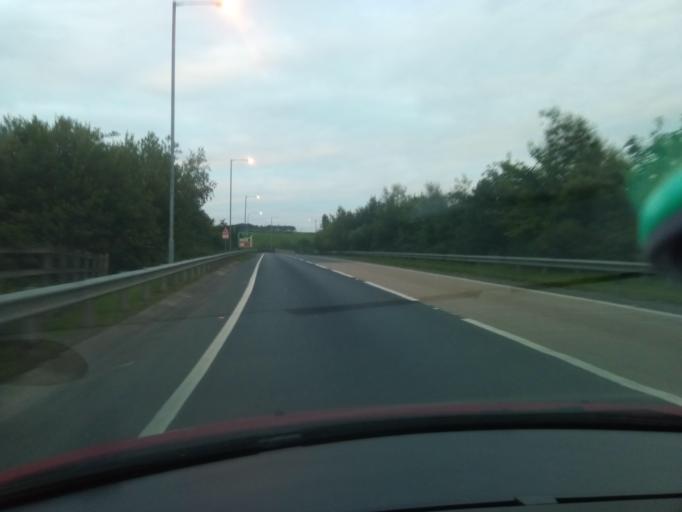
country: GB
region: England
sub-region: Northumberland
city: Haltwhistle
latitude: 54.9675
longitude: -2.4497
